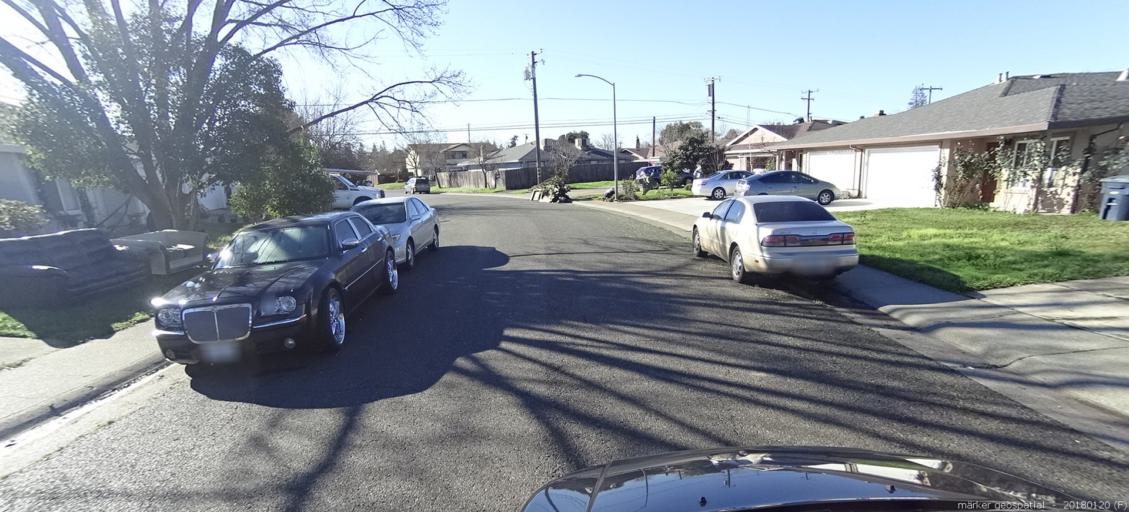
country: US
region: California
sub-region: Sacramento County
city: Rancho Cordova
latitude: 38.5711
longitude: -121.3158
